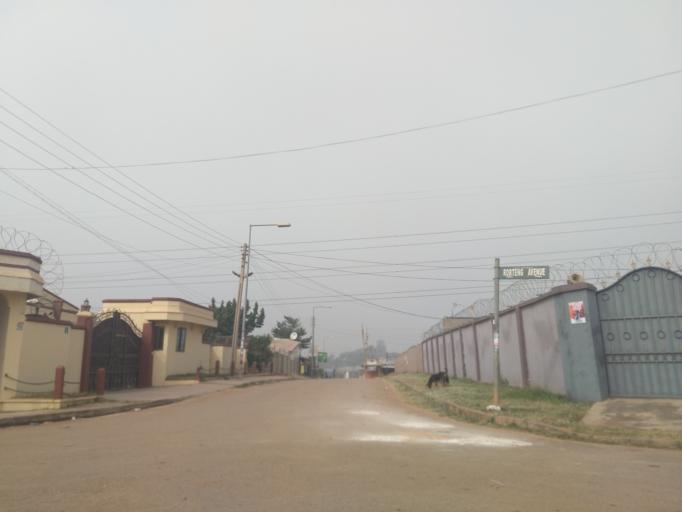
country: GH
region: Ashanti
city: Kumasi
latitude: 6.6627
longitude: -1.6141
